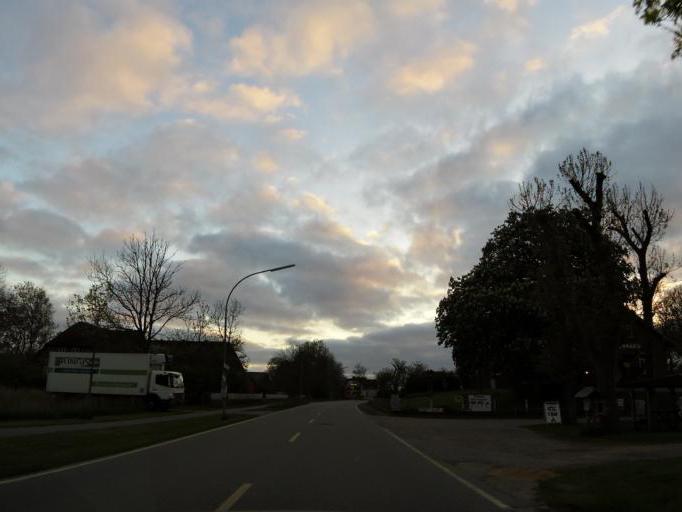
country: DE
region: Schleswig-Holstein
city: Ockholm
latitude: 54.6652
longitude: 8.8290
